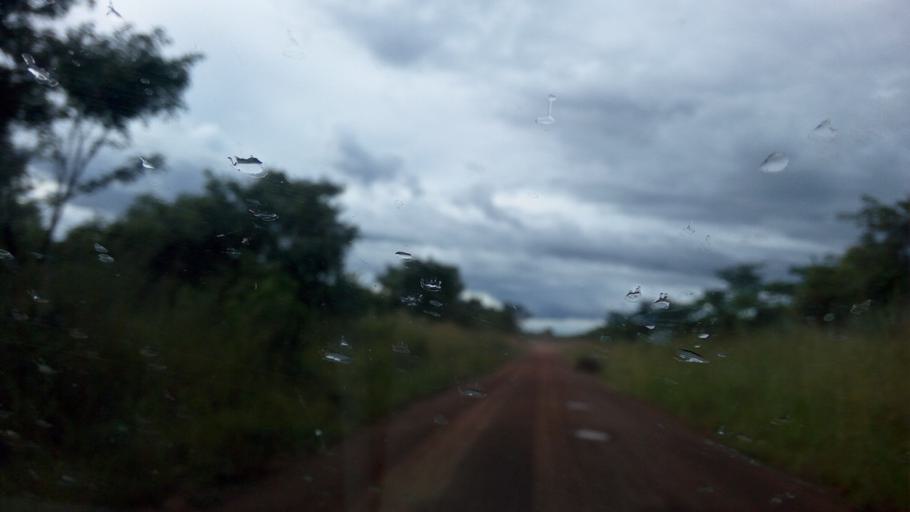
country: ZM
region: Luapula
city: Mwense
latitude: -10.3119
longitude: 28.1142
